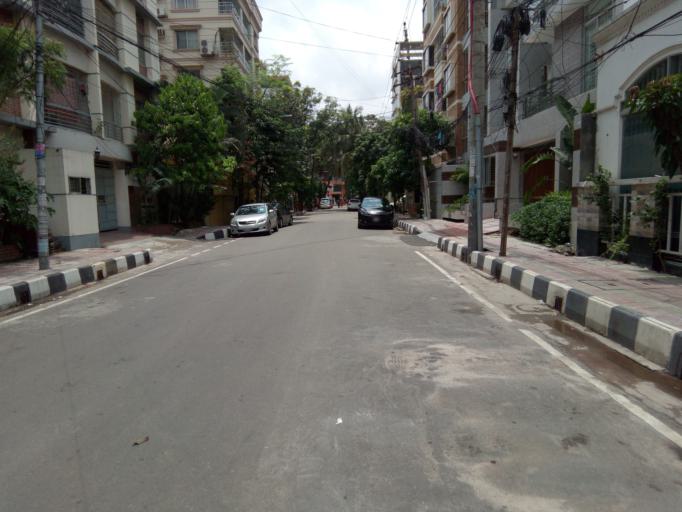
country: BD
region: Dhaka
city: Paltan
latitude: 23.7916
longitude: 90.4093
